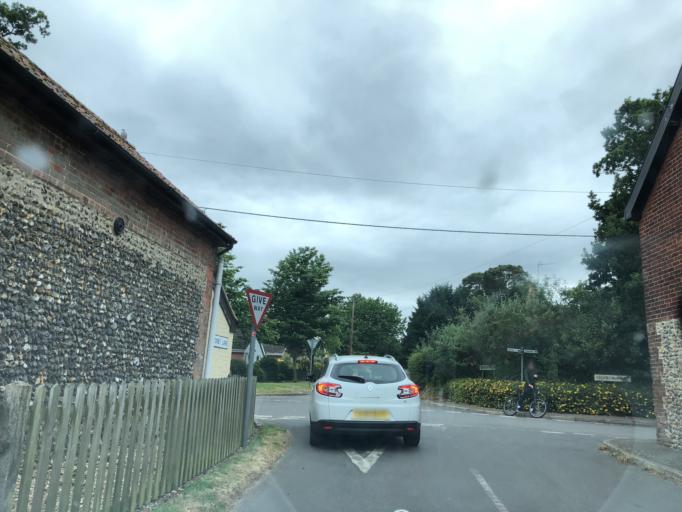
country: GB
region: England
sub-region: Suffolk
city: Thurston
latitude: 52.2500
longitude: 0.8245
